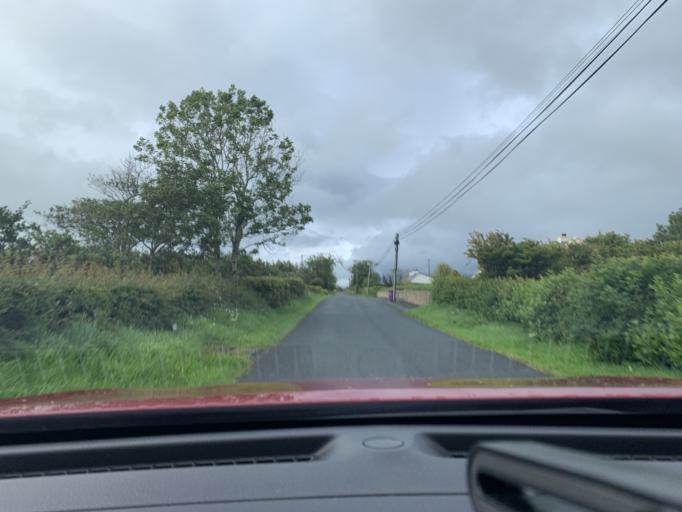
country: IE
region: Connaught
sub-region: Sligo
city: Strandhill
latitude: 54.3693
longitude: -8.5471
